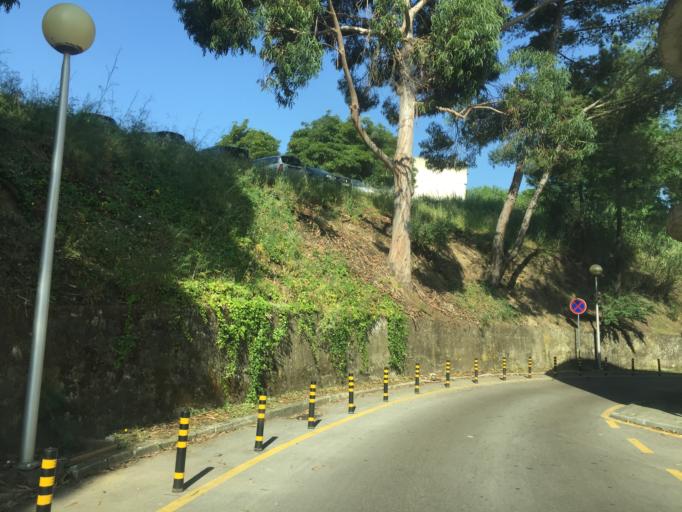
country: PT
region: Lisbon
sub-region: Odivelas
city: Olival do Basto
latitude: 38.7645
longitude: -9.1607
